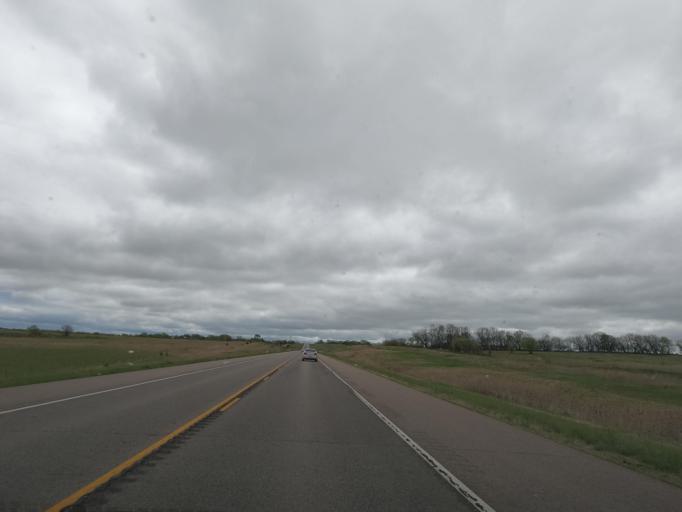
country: US
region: Kansas
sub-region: Elk County
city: Howard
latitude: 37.6363
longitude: -96.3341
